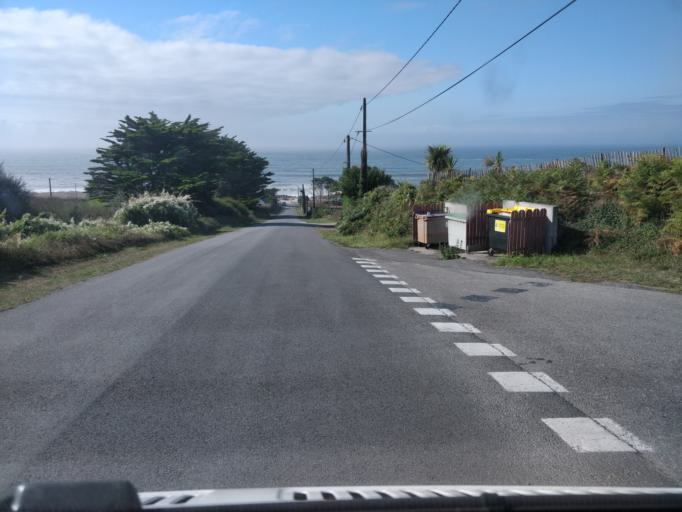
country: FR
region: Brittany
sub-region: Departement du Finistere
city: Plouhinec
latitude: 48.0041
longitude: -4.4970
